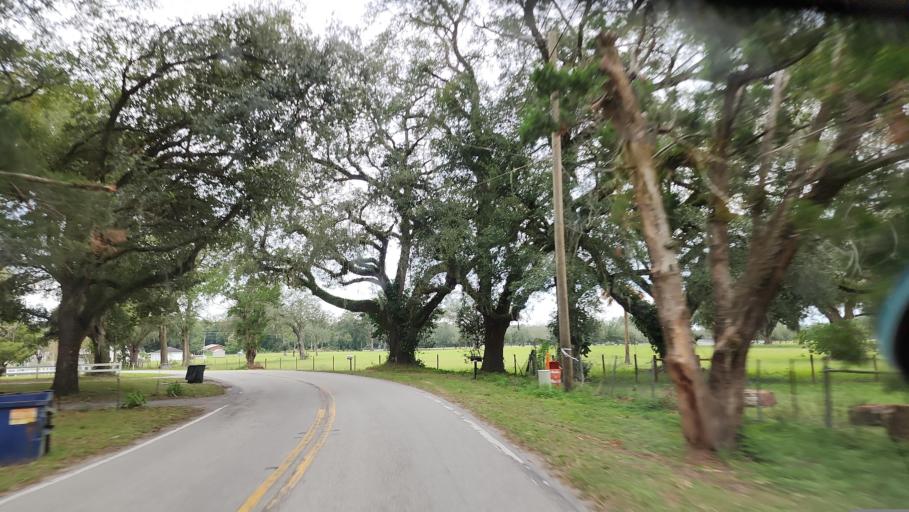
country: US
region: Florida
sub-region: Pasco County
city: Lacoochee
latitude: 28.4645
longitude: -82.1899
